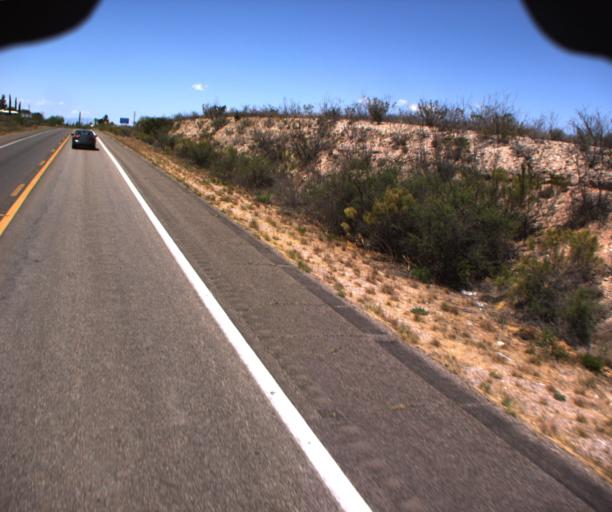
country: US
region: Arizona
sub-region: Cochise County
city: Tombstone
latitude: 31.7054
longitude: -110.0521
